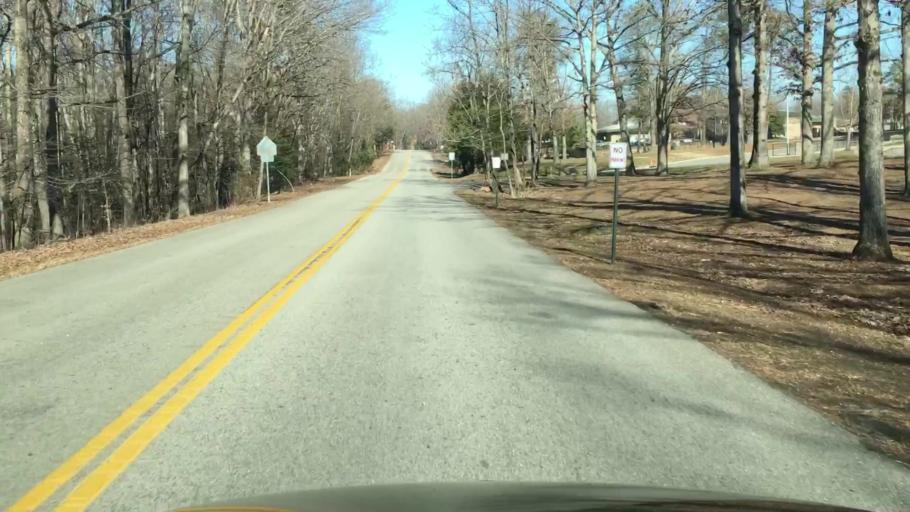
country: US
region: Virginia
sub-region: Chesterfield County
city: Bon Air
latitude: 37.5291
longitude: -77.6149
